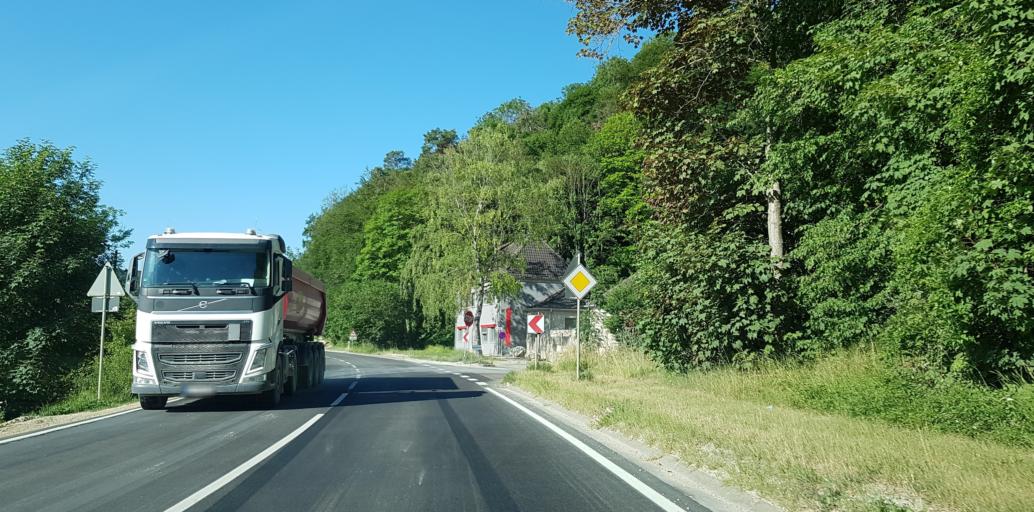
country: DE
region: Baden-Wuerttemberg
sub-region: Tuebingen Region
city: Blaubeuren
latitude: 48.4163
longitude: 9.8658
